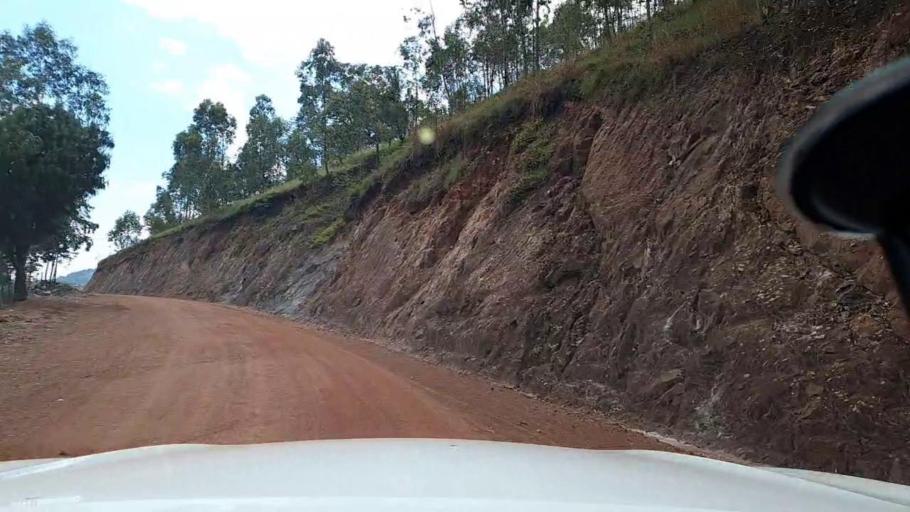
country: RW
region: Kigali
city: Kigali
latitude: -1.7589
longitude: 29.8452
